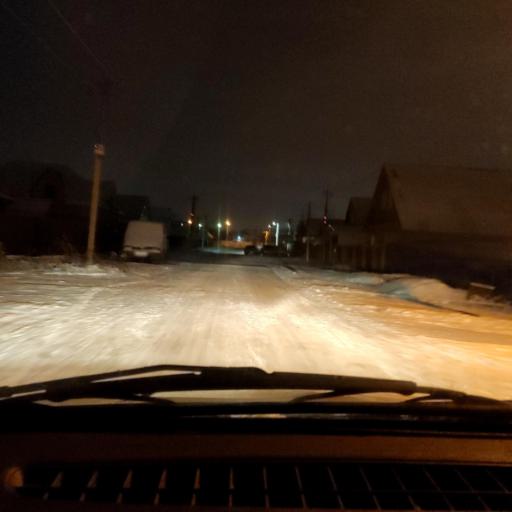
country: RU
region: Bashkortostan
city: Ufa
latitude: 54.6171
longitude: 55.9370
